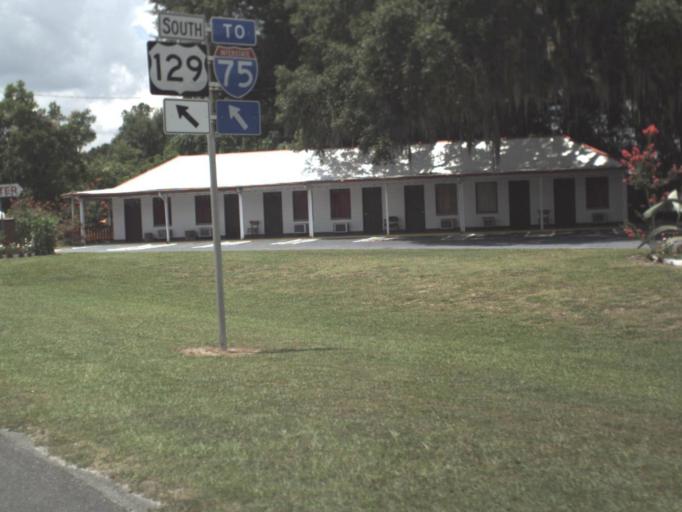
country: US
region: Florida
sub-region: Hamilton County
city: Jasper
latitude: 30.4878
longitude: -82.9292
